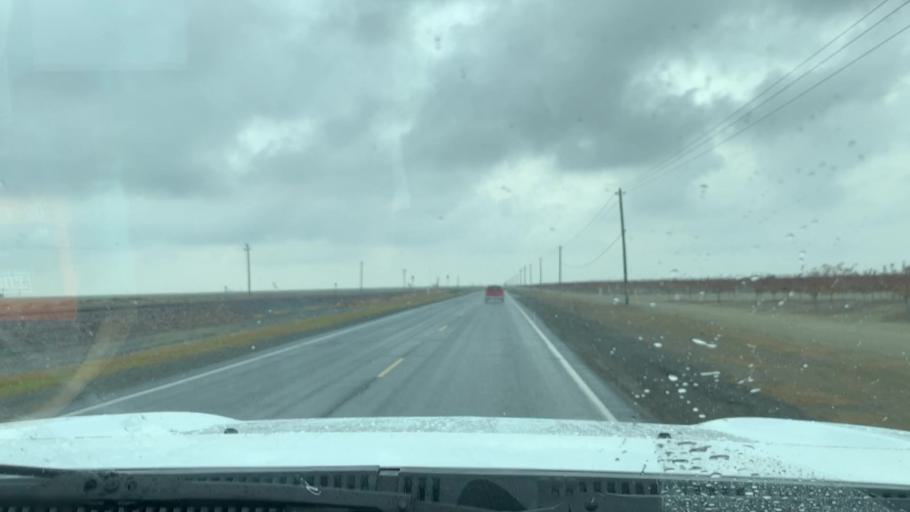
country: US
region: California
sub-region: Tulare County
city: Alpaugh
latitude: 35.9954
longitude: -119.4812
